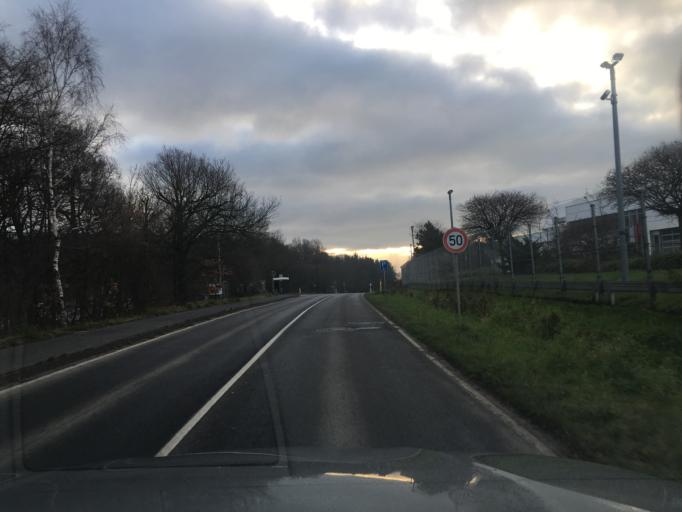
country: DE
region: North Rhine-Westphalia
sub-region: Regierungsbezirk Koln
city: Wachtberg
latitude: 50.6187
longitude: 7.1307
